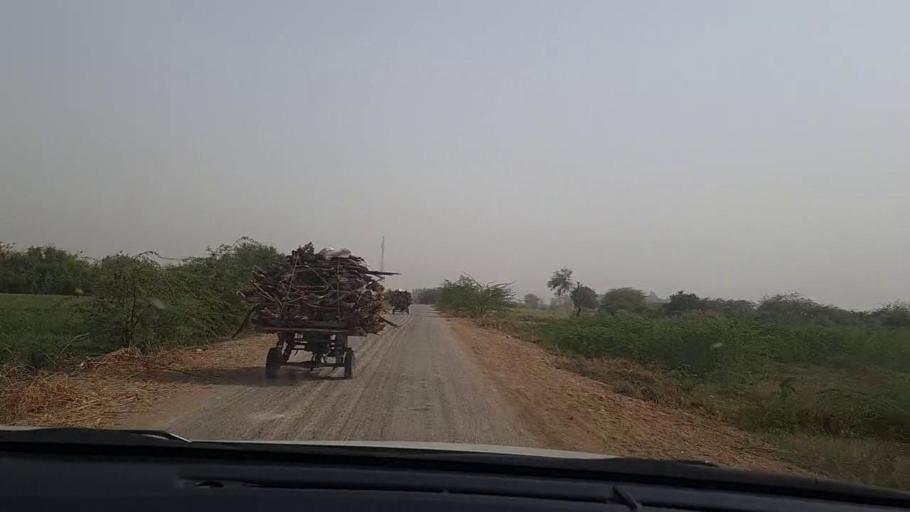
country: PK
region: Sindh
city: Samaro
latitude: 25.3846
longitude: 69.3286
